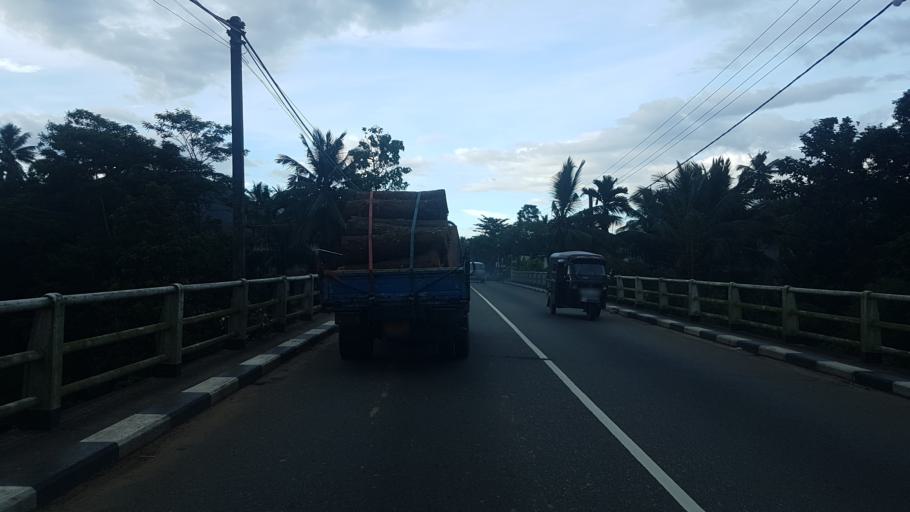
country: LK
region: Western
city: Hanwella Ihala
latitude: 7.0201
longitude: 80.2629
